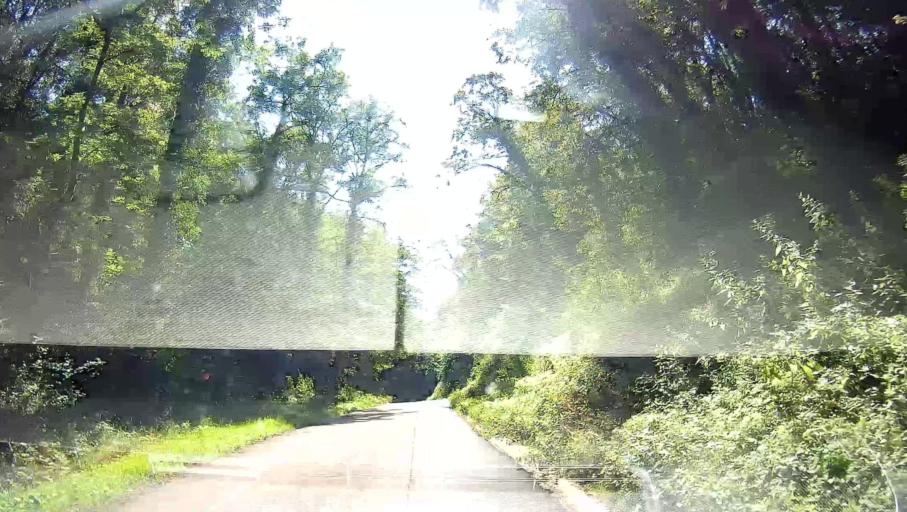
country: FR
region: Bourgogne
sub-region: Departement de la Cote-d'Or
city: Nolay
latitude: 46.9783
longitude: 4.6568
